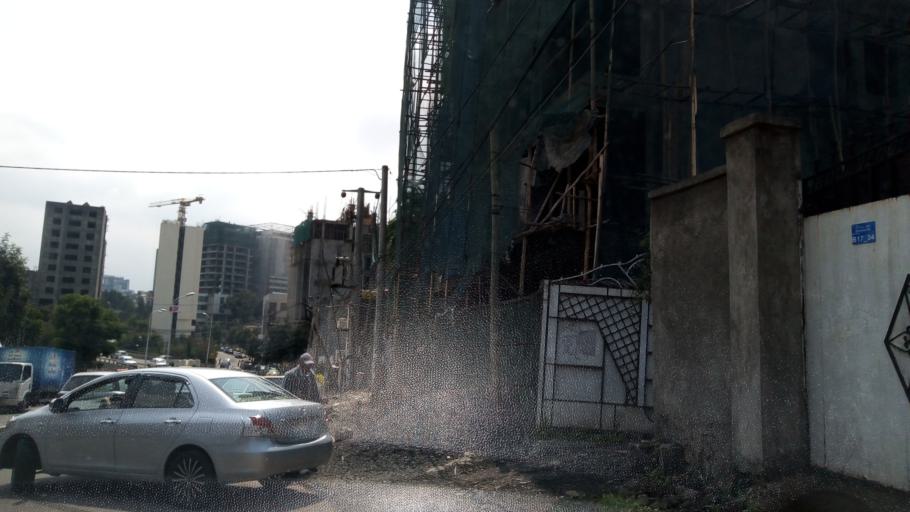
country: ET
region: Adis Abeba
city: Addis Ababa
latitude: 8.9895
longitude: 38.7779
